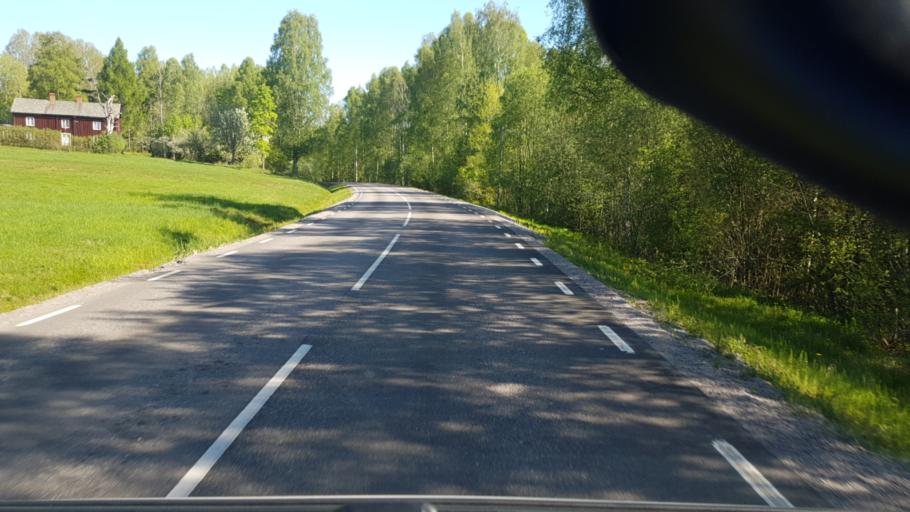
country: SE
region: Vaermland
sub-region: Eda Kommun
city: Amotfors
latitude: 59.7052
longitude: 12.4353
